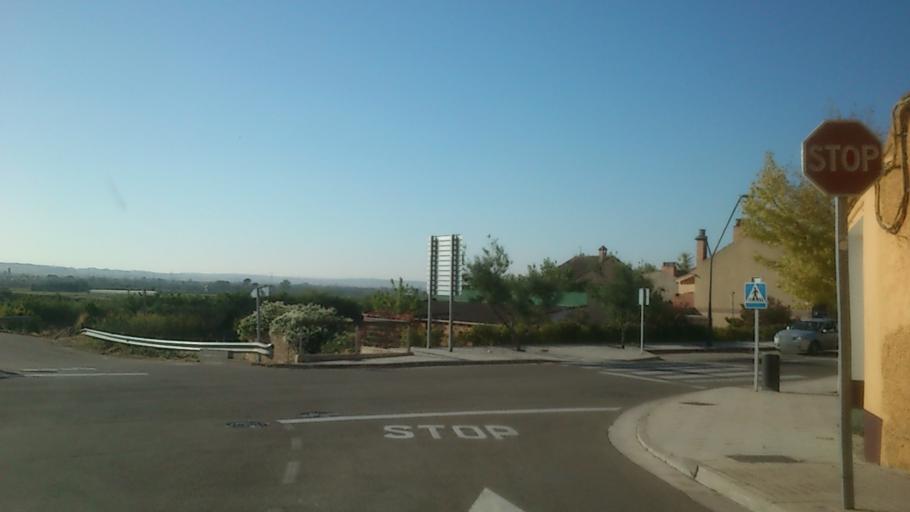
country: ES
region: Aragon
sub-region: Provincia de Zaragoza
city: Villanueva de Gallego
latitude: 41.7709
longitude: -0.8222
